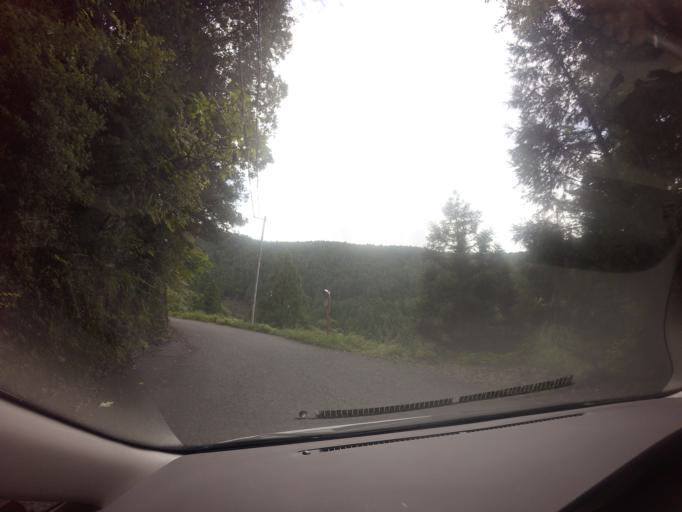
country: JP
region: Wakayama
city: Shingu
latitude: 33.9625
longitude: 135.8496
